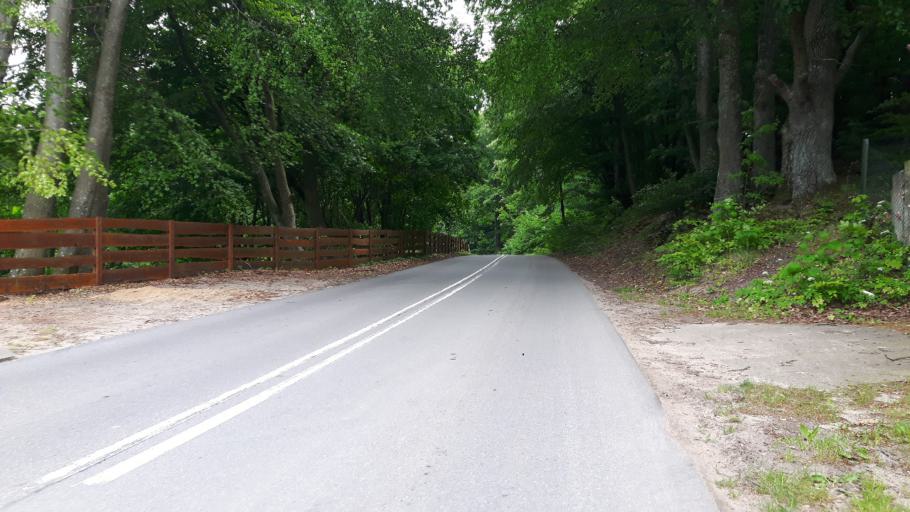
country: PL
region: Pomeranian Voivodeship
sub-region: Powiat leborski
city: Leba
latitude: 54.7551
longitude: 17.7028
